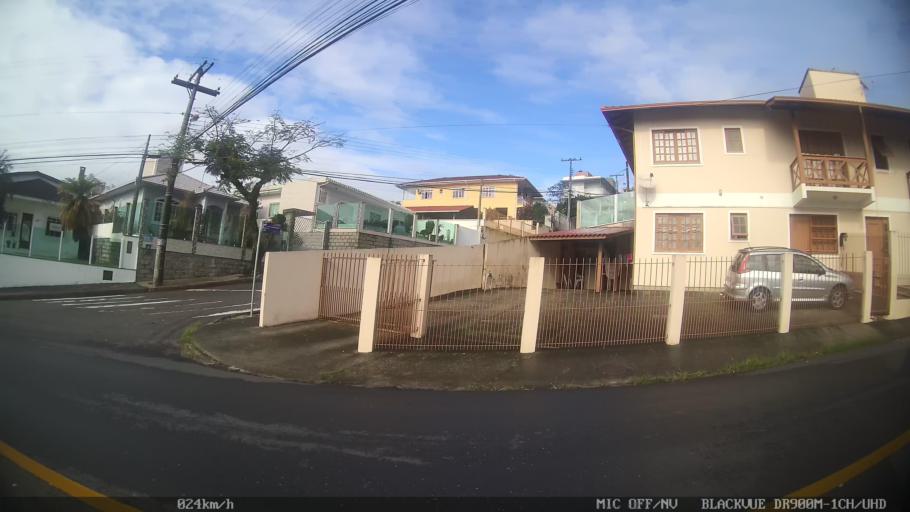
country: BR
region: Santa Catarina
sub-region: Sao Jose
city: Campinas
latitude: -27.6139
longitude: -48.6320
